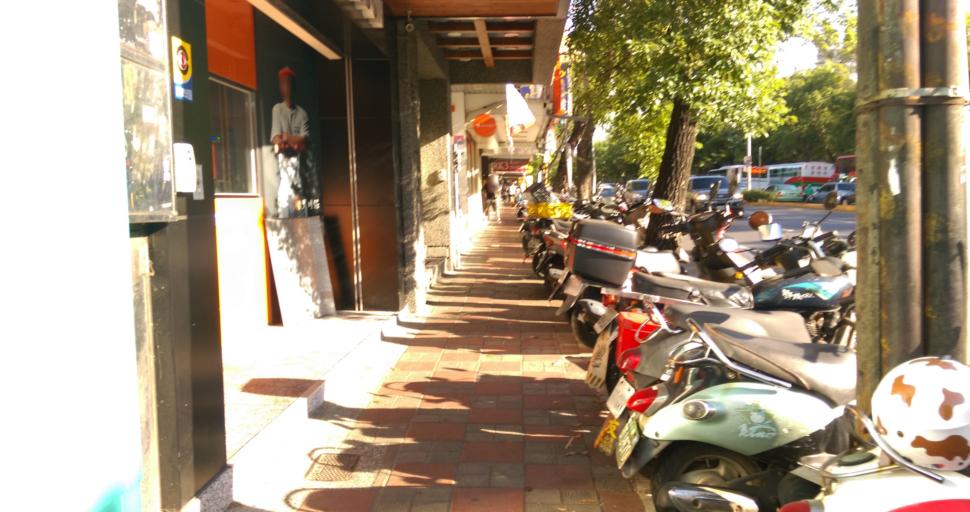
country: TW
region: Taiwan
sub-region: Hsinchu
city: Hsinchu
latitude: 24.7961
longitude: 120.9980
